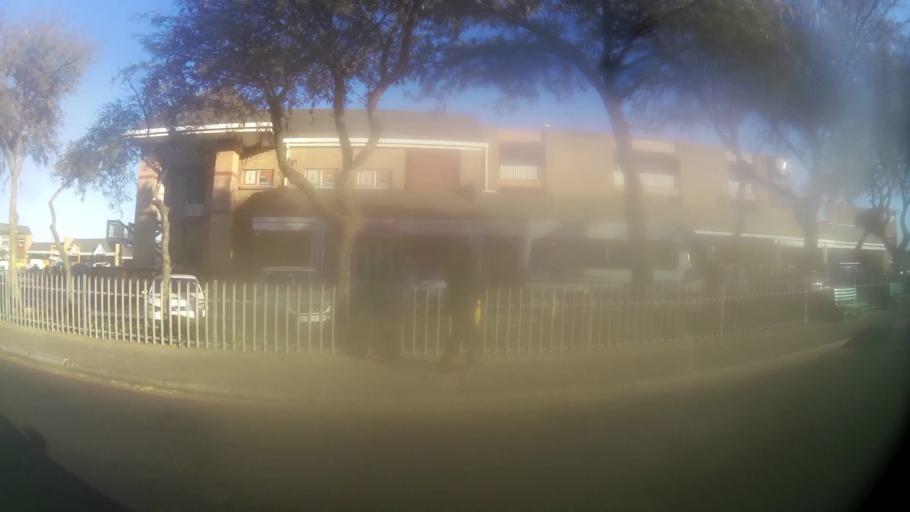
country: ZA
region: Gauteng
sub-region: City of Johannesburg Metropolitan Municipality
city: Midrand
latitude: -25.9963
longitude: 28.1282
